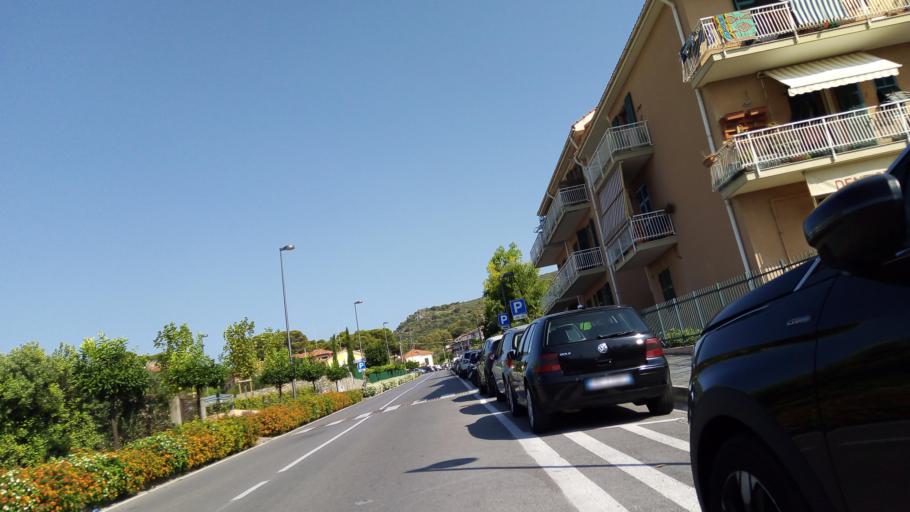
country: IT
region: Liguria
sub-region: Provincia di Savona
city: Borgio
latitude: 44.1601
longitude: 8.3060
